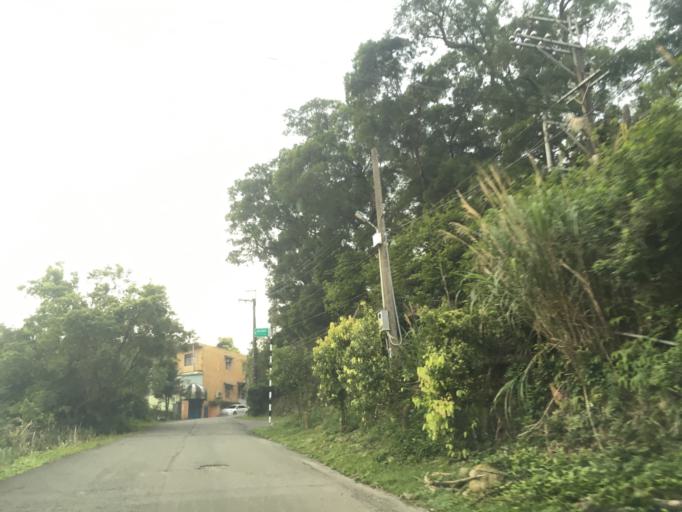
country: TW
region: Taiwan
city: Daxi
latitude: 24.8840
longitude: 121.3000
